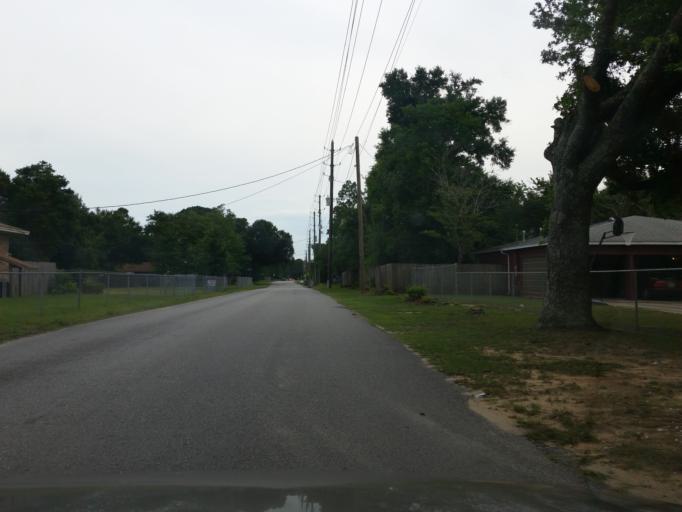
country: US
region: Florida
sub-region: Escambia County
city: Ferry Pass
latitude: 30.4919
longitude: -87.2052
